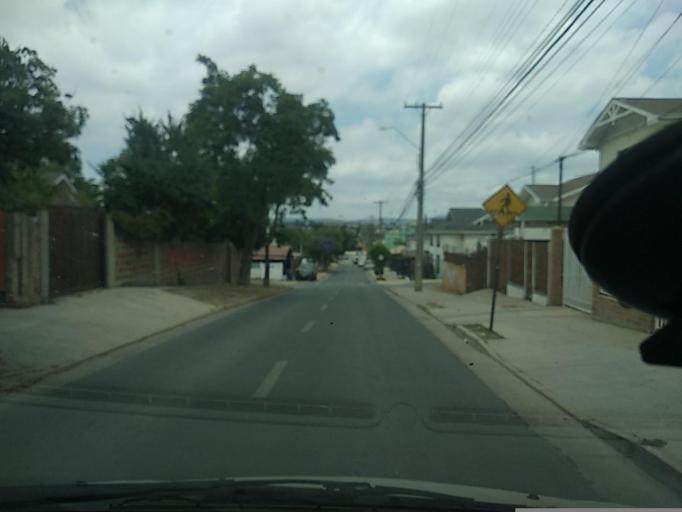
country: CL
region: Valparaiso
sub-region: Provincia de Marga Marga
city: Villa Alemana
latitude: -33.0367
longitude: -71.4043
